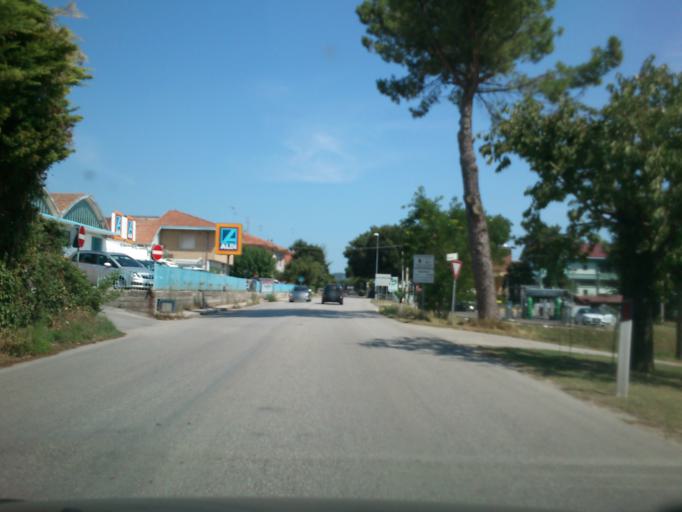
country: IT
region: The Marches
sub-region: Provincia di Pesaro e Urbino
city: Lucrezia
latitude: 43.7684
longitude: 12.9315
